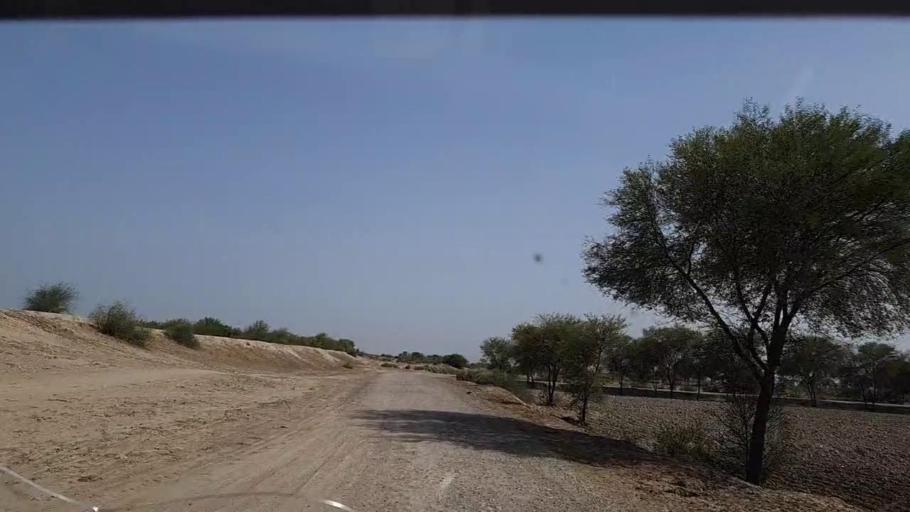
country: PK
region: Sindh
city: Phulji
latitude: 26.9271
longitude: 67.6846
